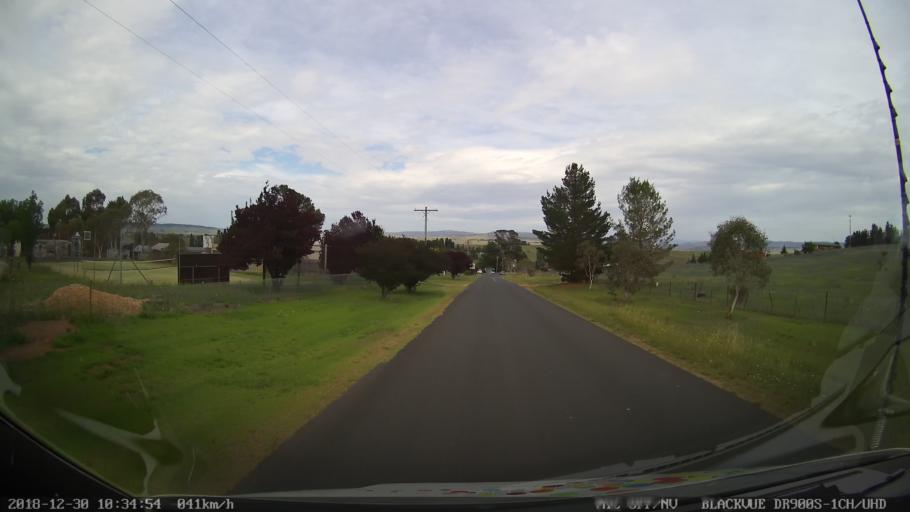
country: AU
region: New South Wales
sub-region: Snowy River
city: Berridale
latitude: -36.5021
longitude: 148.8372
